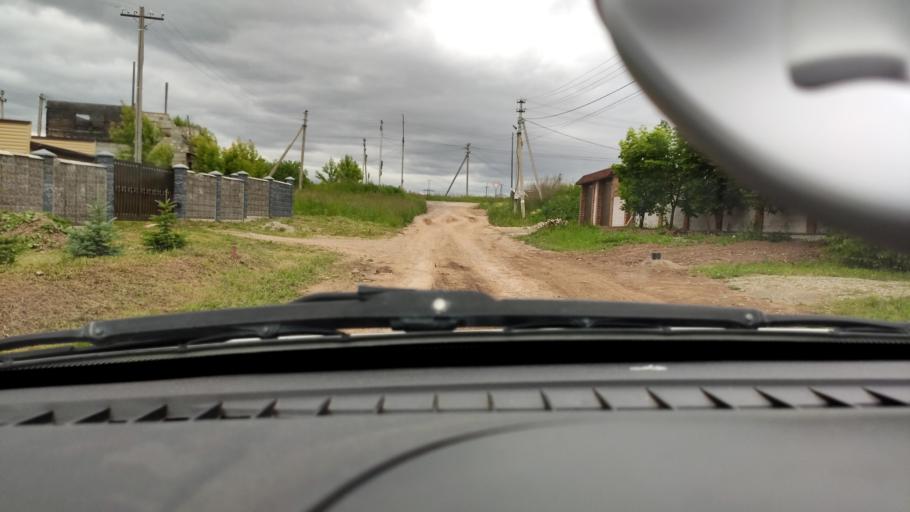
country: RU
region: Perm
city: Ferma
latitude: 57.9125
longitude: 56.3138
